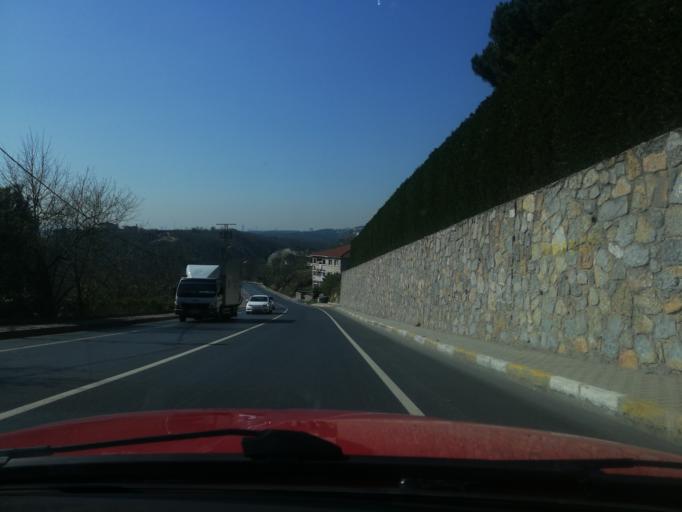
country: TR
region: Istanbul
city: Umraniye
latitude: 41.0746
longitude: 29.1488
